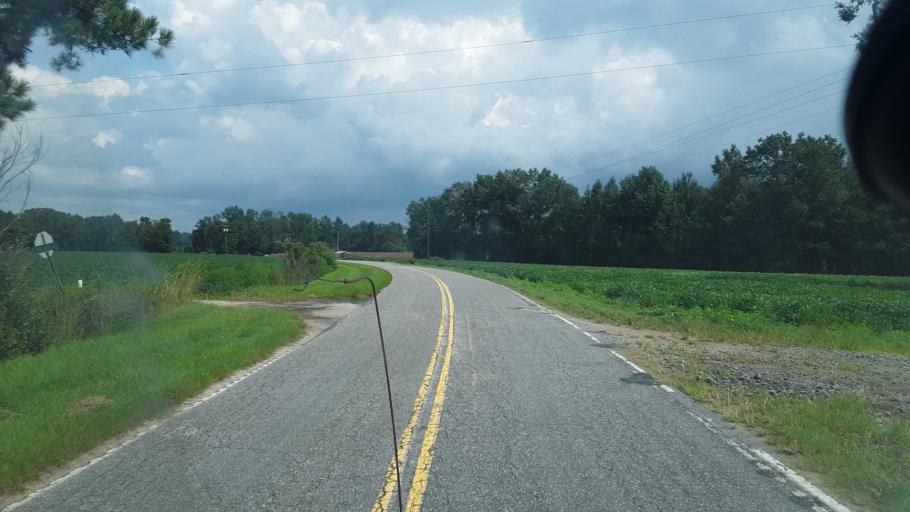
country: US
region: South Carolina
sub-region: Lee County
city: Bishopville
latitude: 34.1785
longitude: -80.1552
